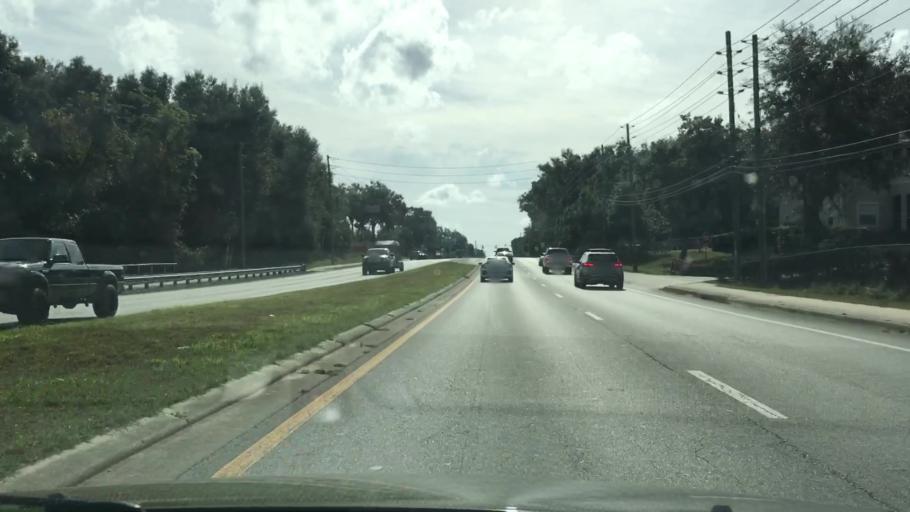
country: US
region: Florida
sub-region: Volusia County
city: North DeLand
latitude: 29.0457
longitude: -81.3248
